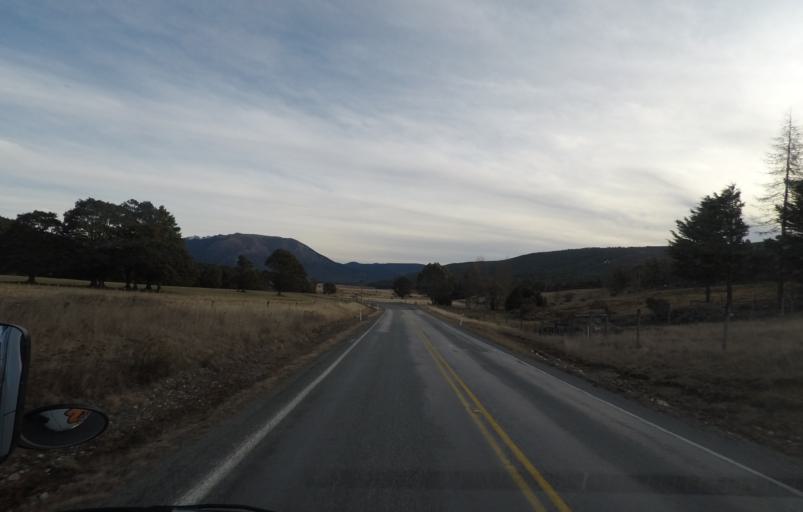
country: NZ
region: Tasman
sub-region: Tasman District
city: Wakefield
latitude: -41.7876
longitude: 172.8871
